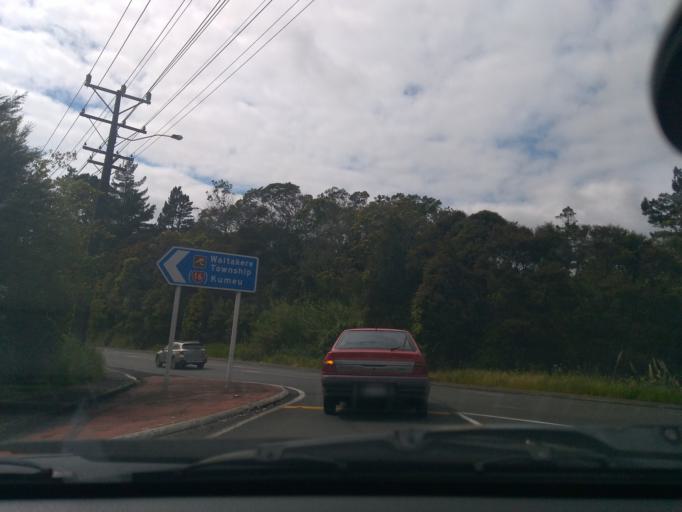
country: NZ
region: Auckland
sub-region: Auckland
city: Rosebank
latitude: -36.8649
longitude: 174.5666
